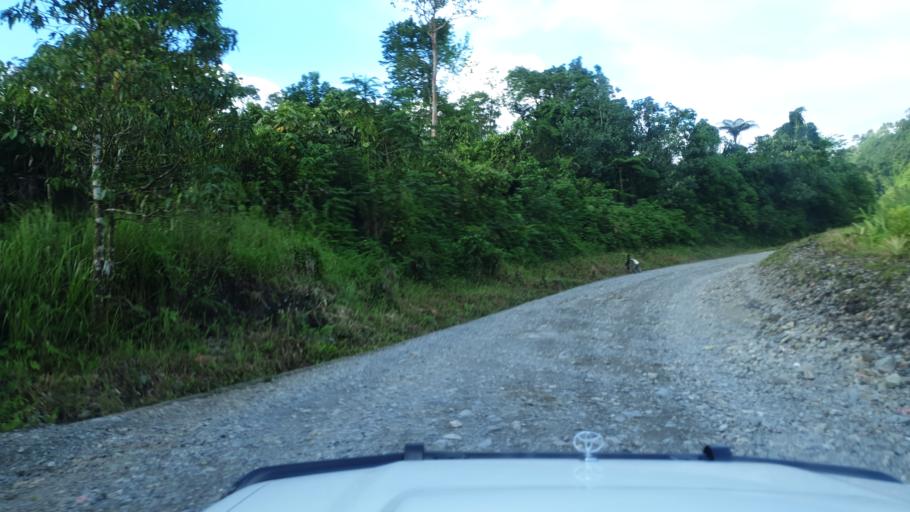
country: PG
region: Bougainville
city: Panguna
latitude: -6.3793
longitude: 155.4336
